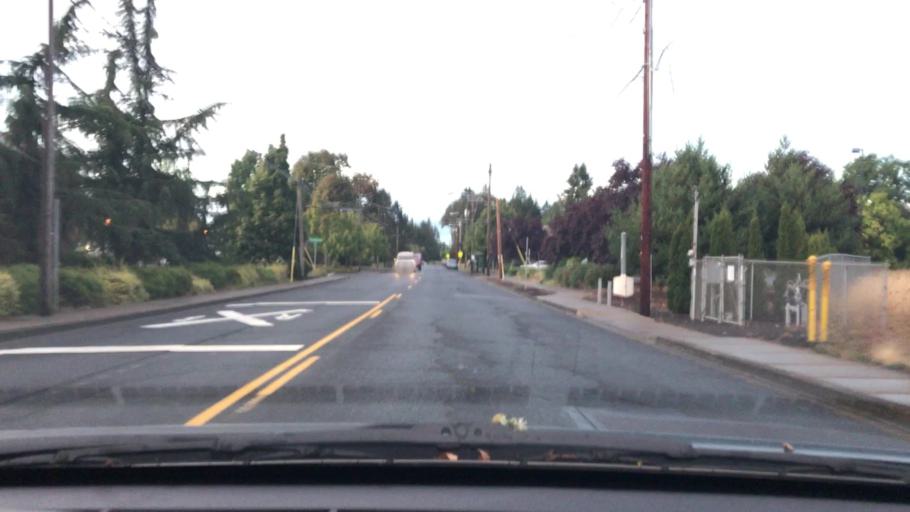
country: US
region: Oregon
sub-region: Yamhill County
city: McMinnville
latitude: 45.1996
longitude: -123.1953
